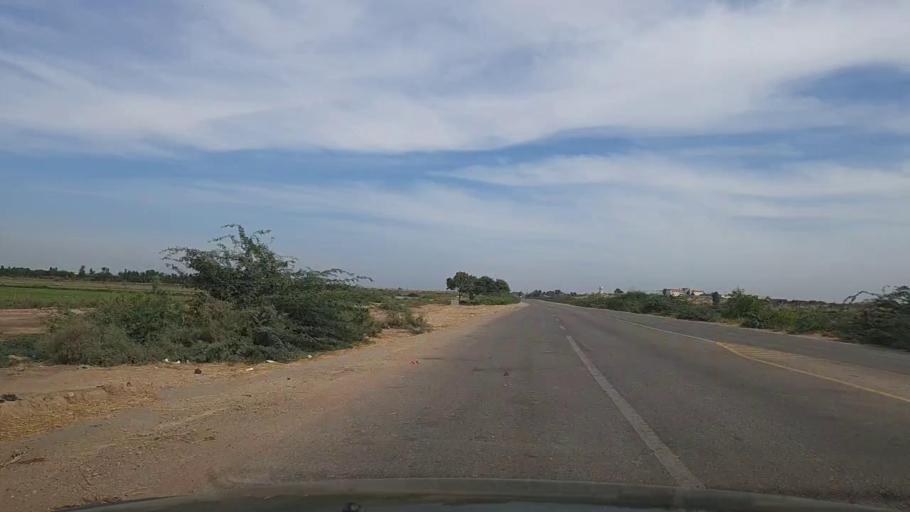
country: PK
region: Sindh
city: Thatta
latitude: 24.8135
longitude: 67.9782
